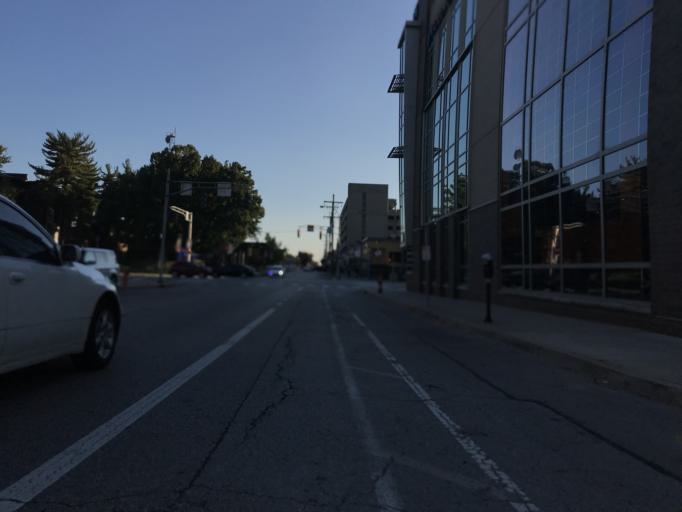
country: US
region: Kentucky
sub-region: Jefferson County
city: Louisville
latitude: 38.2459
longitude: -85.7497
